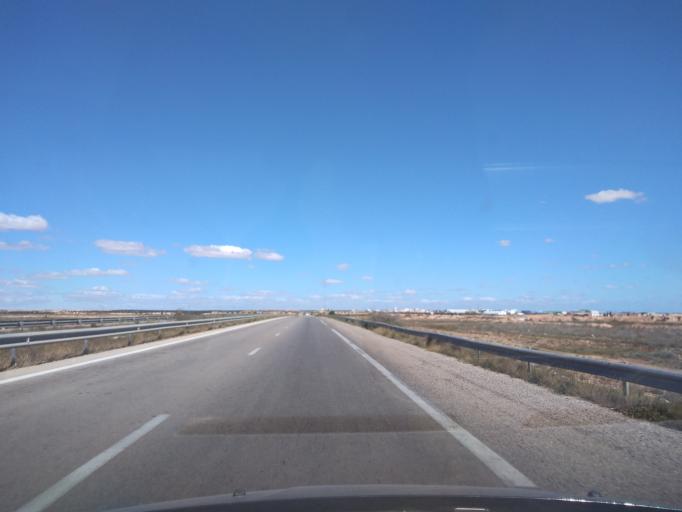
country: TN
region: Safaqis
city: Al Qarmadah
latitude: 34.9176
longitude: 10.7375
